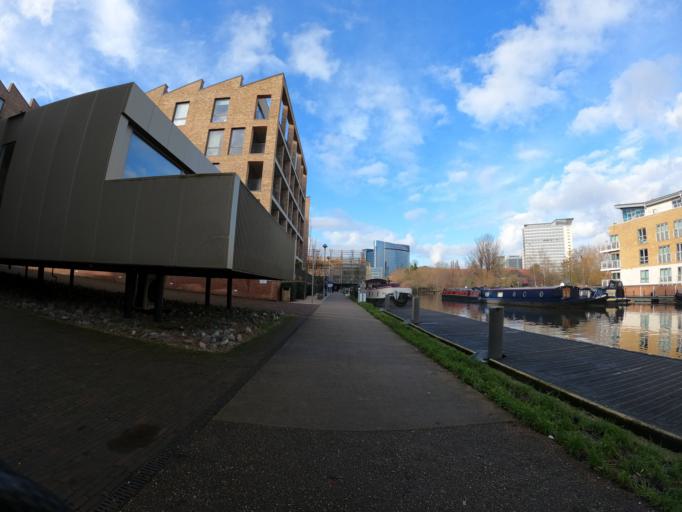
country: GB
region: England
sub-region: Greater London
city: Brentford
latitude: 51.4844
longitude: -0.3129
